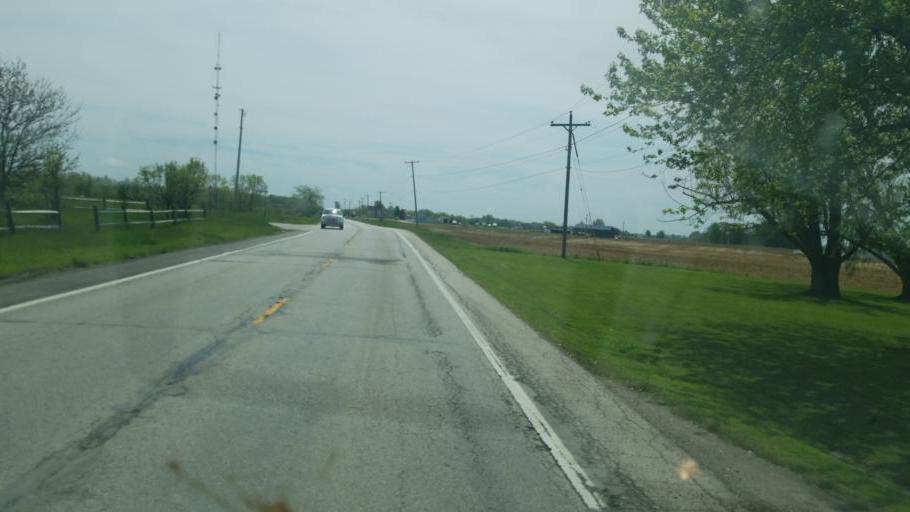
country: US
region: Ohio
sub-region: Ottawa County
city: Oak Harbor
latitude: 41.5806
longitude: -83.0922
